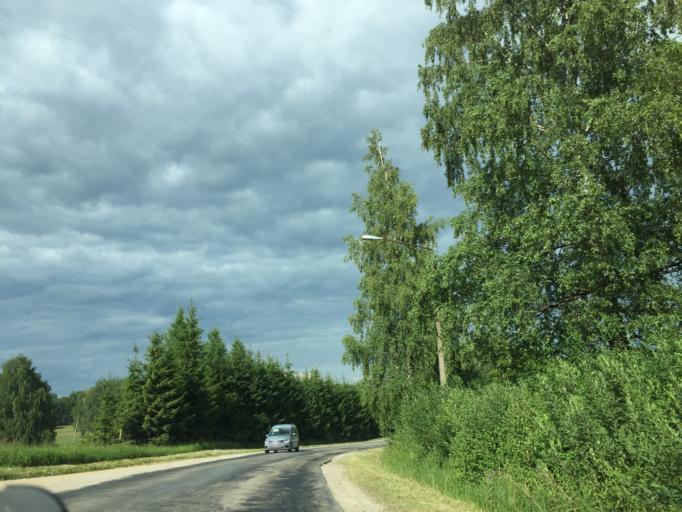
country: LV
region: Skriveri
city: Skriveri
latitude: 56.8432
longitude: 25.1475
